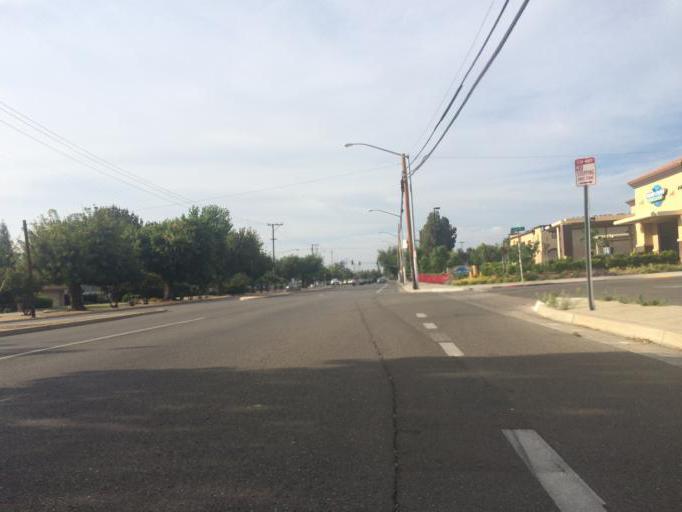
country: US
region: California
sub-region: Fresno County
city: Fresno
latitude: 36.7924
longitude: -119.7722
